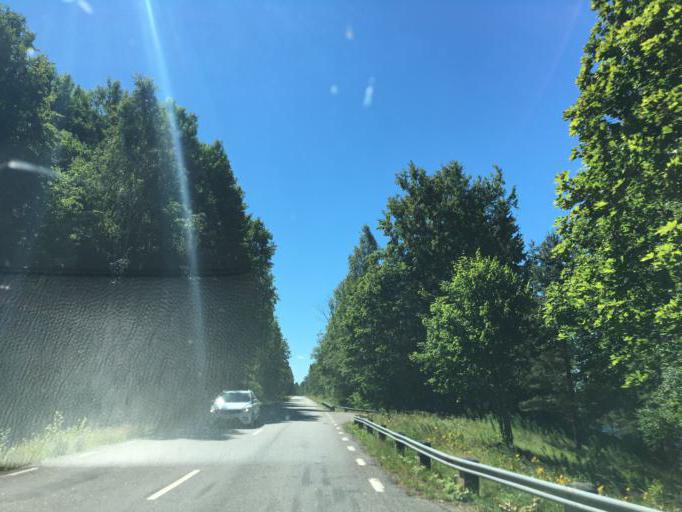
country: SE
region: OErebro
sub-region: Laxa Kommun
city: Laxa
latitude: 58.8332
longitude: 14.5463
